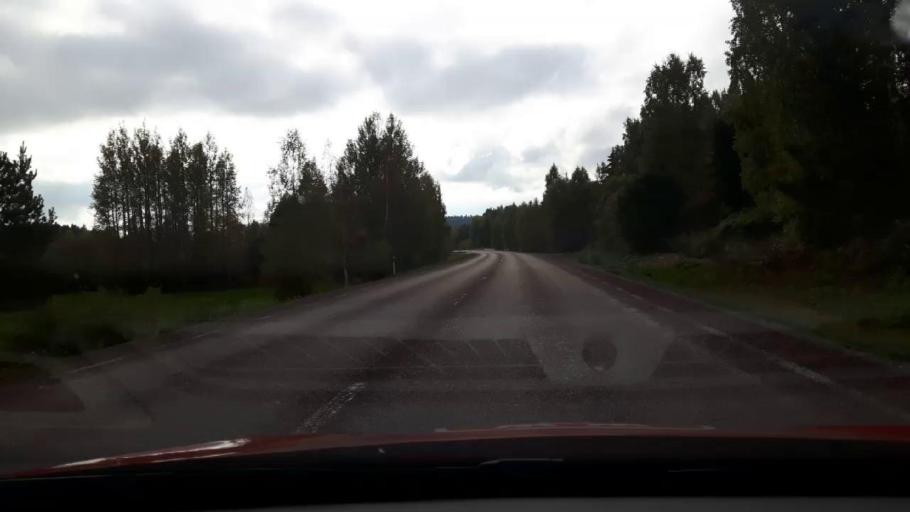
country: SE
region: Gaevleborg
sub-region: Ljusdals Kommun
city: Jaervsoe
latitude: 61.6110
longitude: 16.2952
